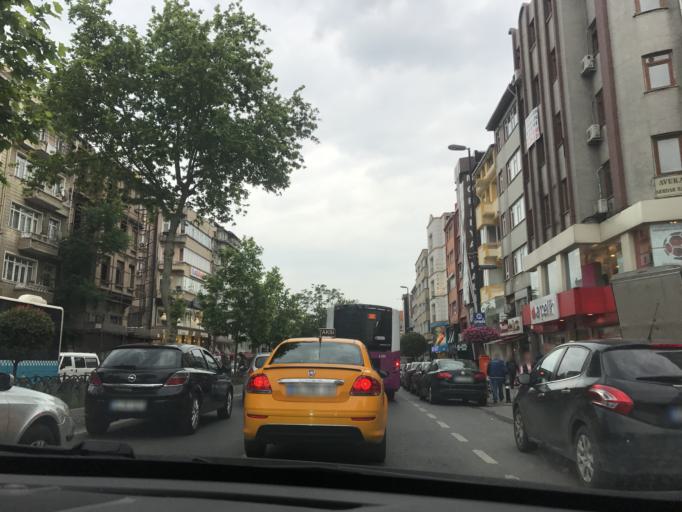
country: TR
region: Istanbul
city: Istanbul
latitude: 41.0245
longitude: 28.9415
